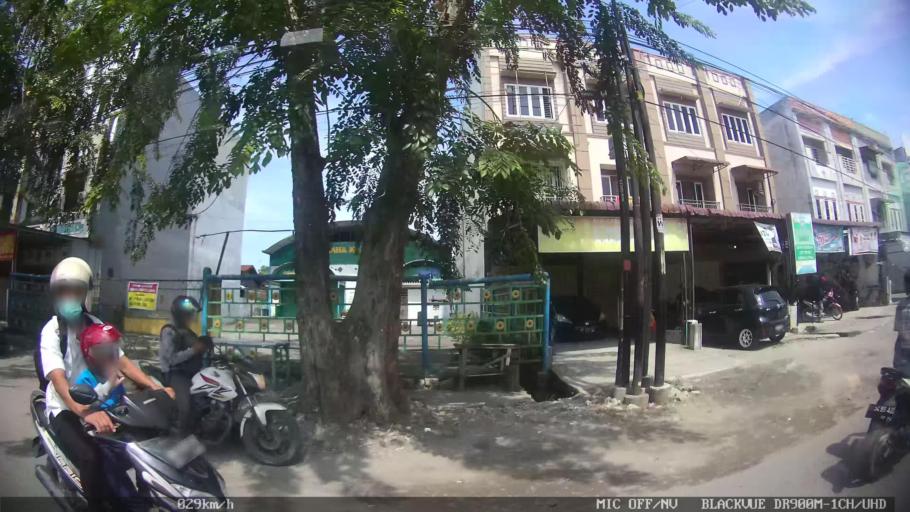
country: ID
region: North Sumatra
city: Labuhan Deli
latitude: 3.6826
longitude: 98.6561
